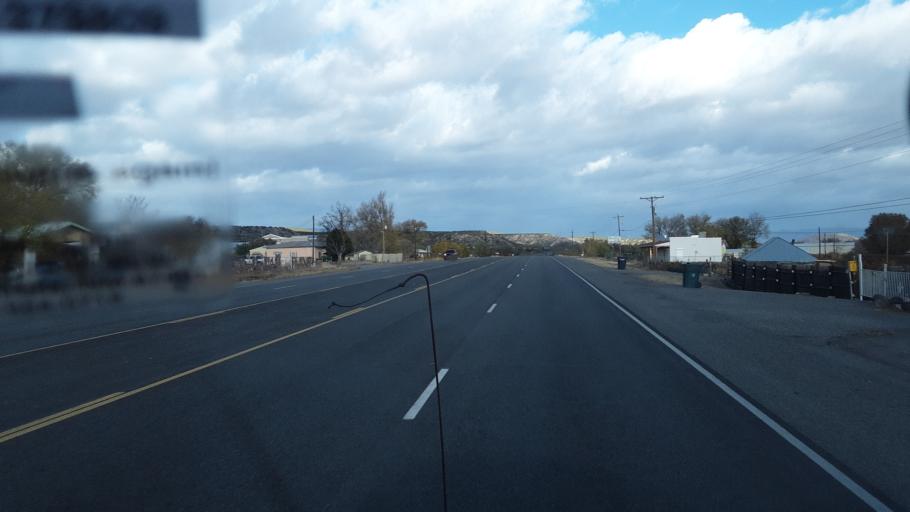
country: US
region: New Mexico
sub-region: Rio Arriba County
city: Ohkay Owingeh
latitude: 36.0439
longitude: -106.1049
